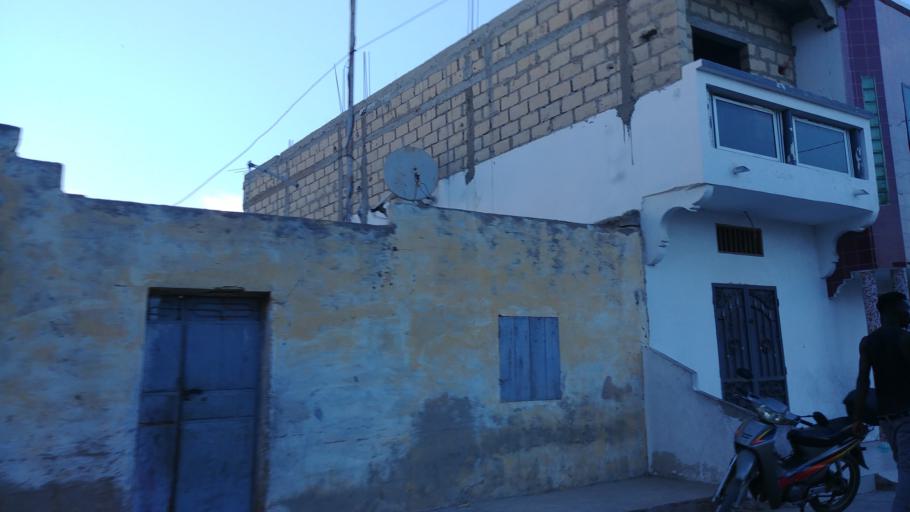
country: SN
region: Saint-Louis
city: Saint-Louis
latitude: 16.0052
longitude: -16.4881
